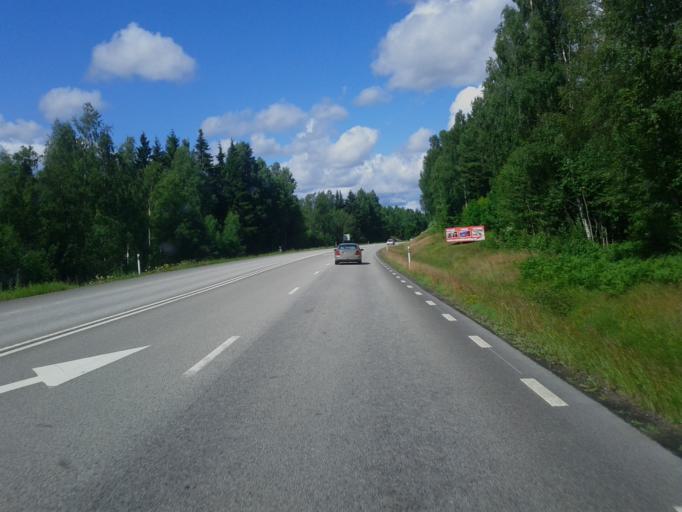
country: SE
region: Dalarna
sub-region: Rattviks Kommun
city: Raettvik
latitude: 60.9021
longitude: 15.0761
